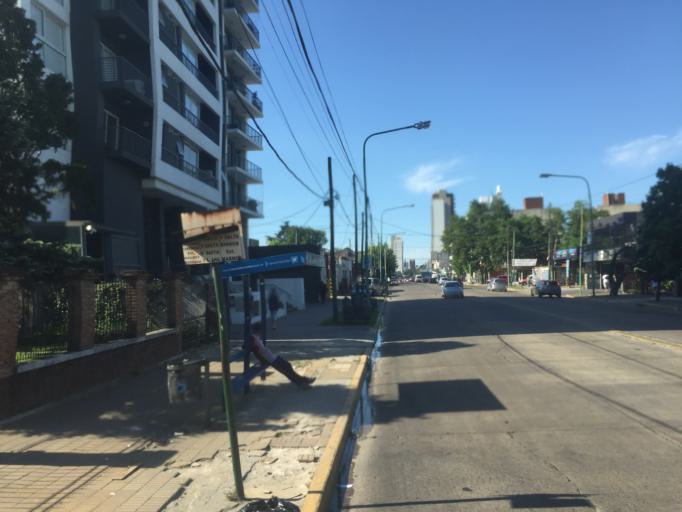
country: AR
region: Buenos Aires
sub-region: Partido de Lomas de Zamora
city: Lomas de Zamora
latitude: -34.7633
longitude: -58.3965
